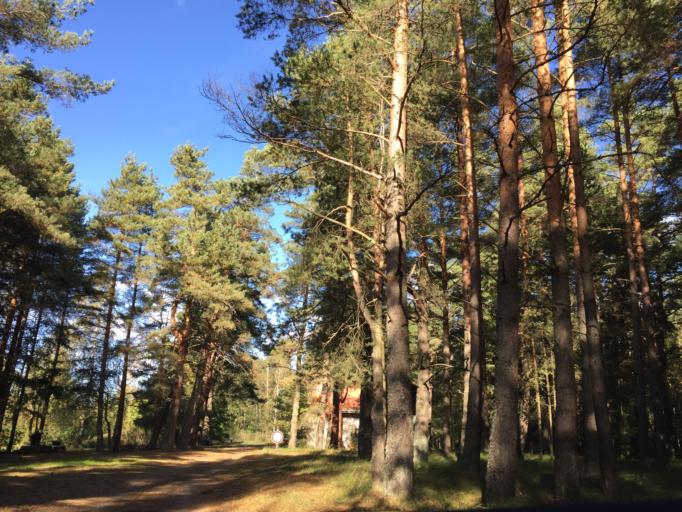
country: LV
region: Mesraga
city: Mersrags
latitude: 57.2592
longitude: 23.1357
